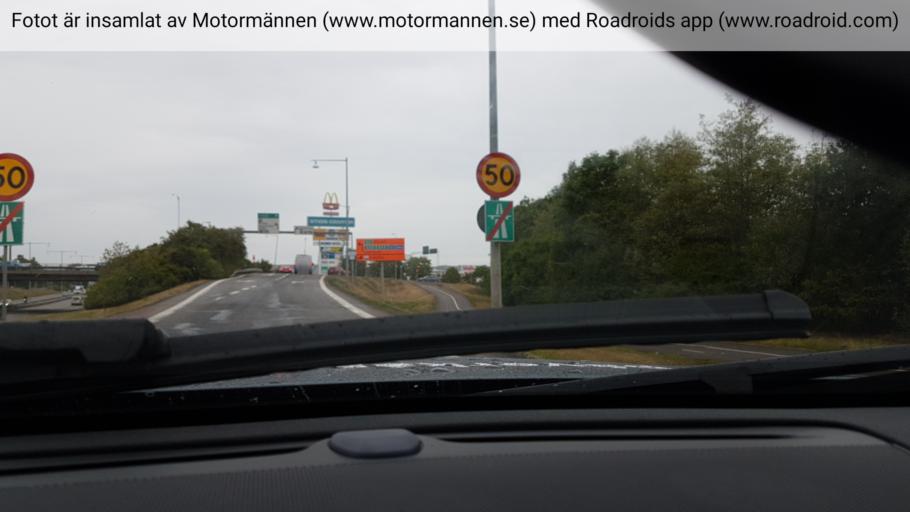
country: SE
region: Vaestra Goetaland
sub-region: Goteborg
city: Goeteborg
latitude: 57.7458
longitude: 11.9907
